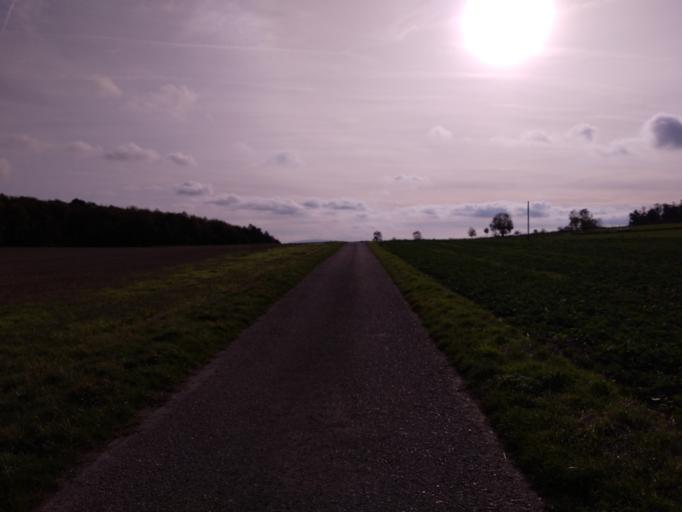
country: DE
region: North Rhine-Westphalia
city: Beverungen
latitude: 51.6918
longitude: 9.3435
